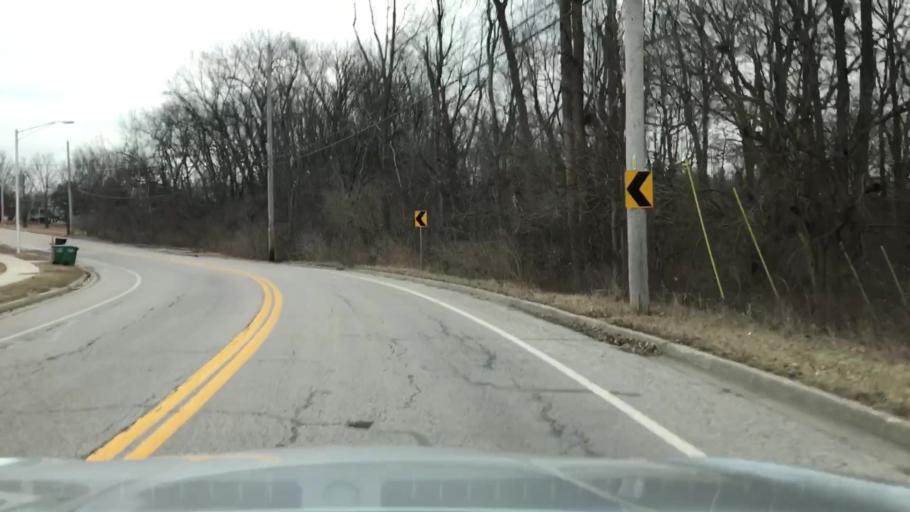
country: US
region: Missouri
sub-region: Jackson County
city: Lees Summit
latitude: 38.8968
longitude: -94.3944
